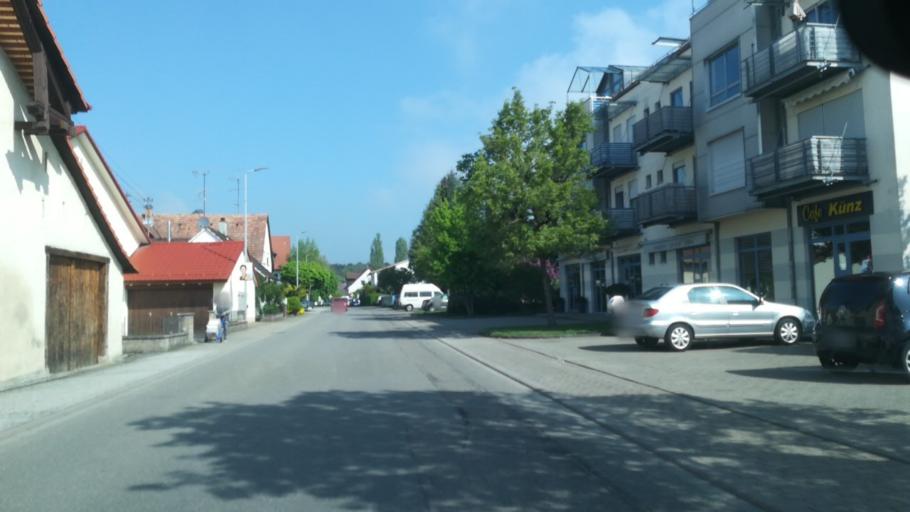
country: DE
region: Baden-Wuerttemberg
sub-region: Freiburg Region
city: Hilzingen
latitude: 47.7656
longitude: 8.7879
